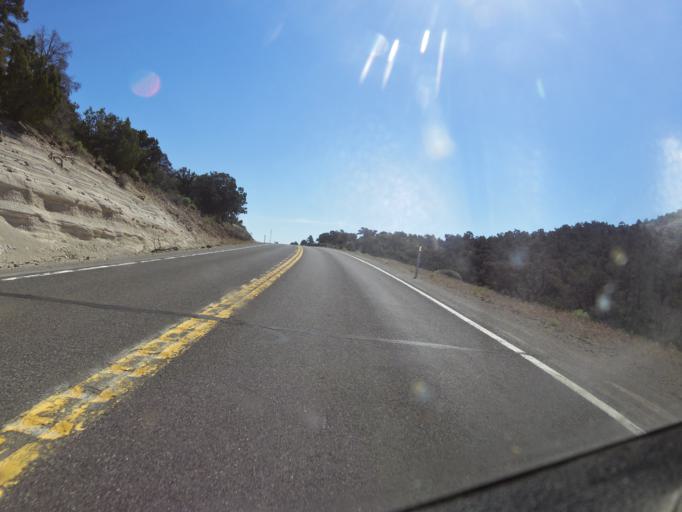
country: US
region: Nevada
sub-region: White Pine County
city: Ely
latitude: 38.8180
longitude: -115.2856
